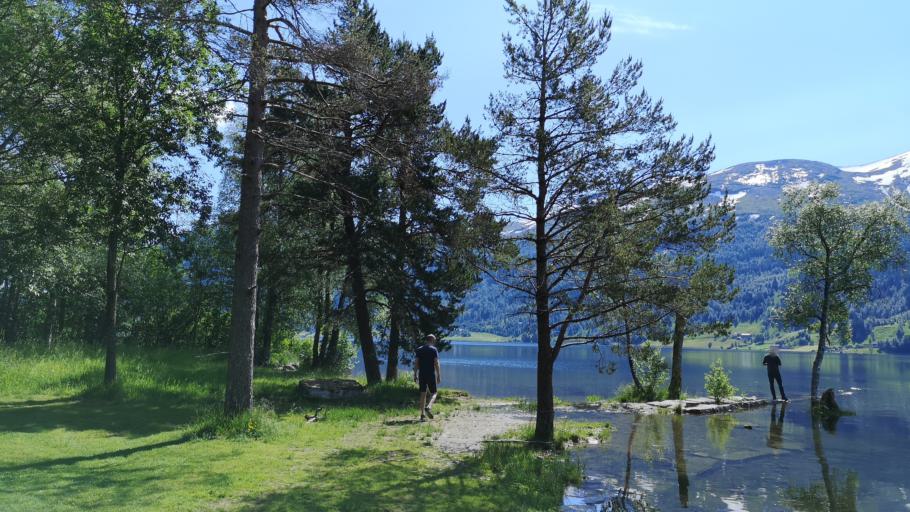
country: NO
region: Sogn og Fjordane
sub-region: Gloppen
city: Sandane
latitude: 61.5106
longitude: 6.1567
